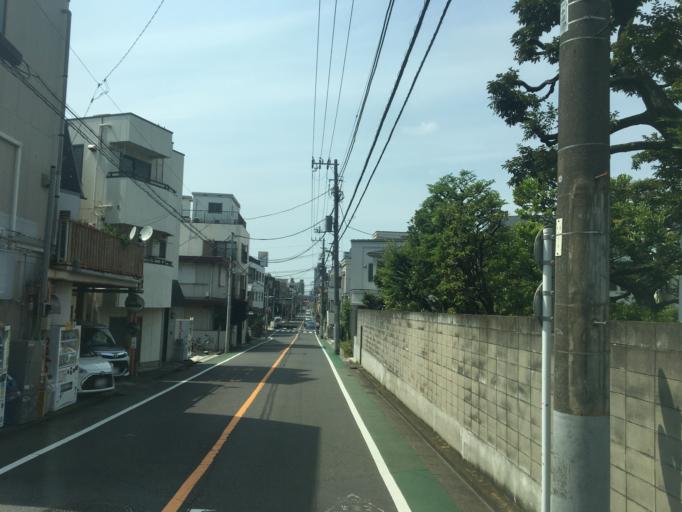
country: JP
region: Tokyo
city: Tokyo
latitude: 35.7424
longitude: 139.7013
